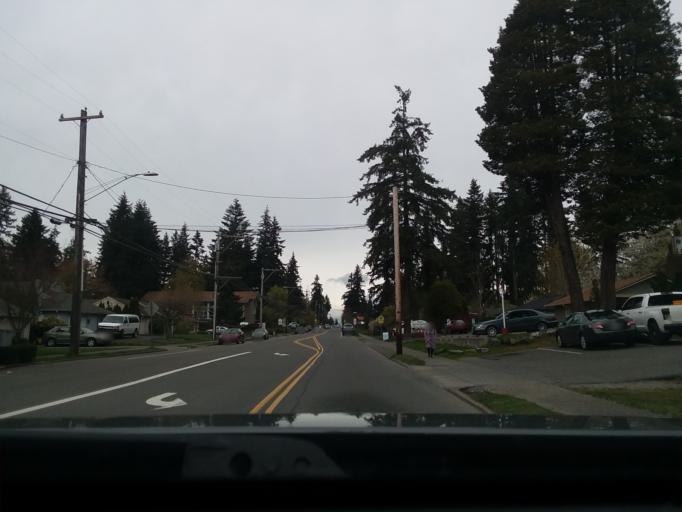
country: US
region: Washington
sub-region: Snohomish County
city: Mountlake Terrace
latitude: 47.7903
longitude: -122.3084
